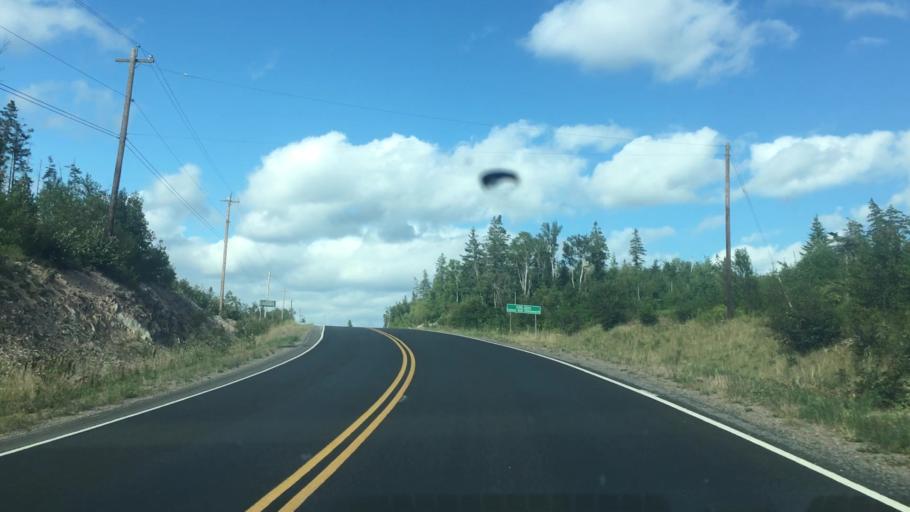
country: CA
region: Nova Scotia
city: Princeville
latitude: 45.8084
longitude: -60.7084
